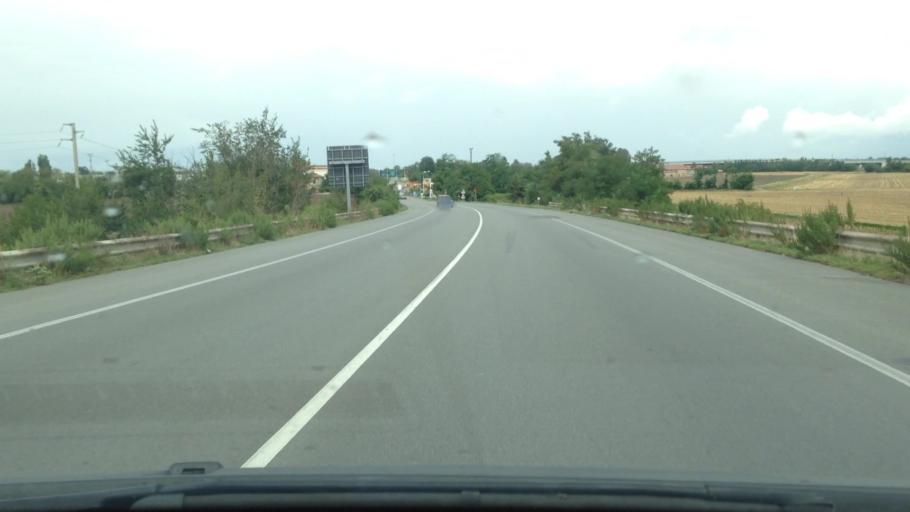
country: IT
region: Piedmont
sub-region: Provincia di Alessandria
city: Tortona
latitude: 44.8977
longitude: 8.8399
